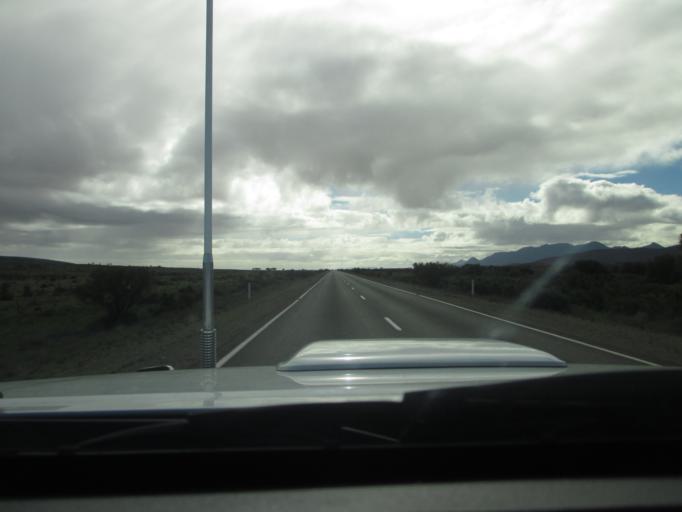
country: AU
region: South Australia
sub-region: Flinders Ranges
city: Quorn
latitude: -31.6397
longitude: 138.3847
